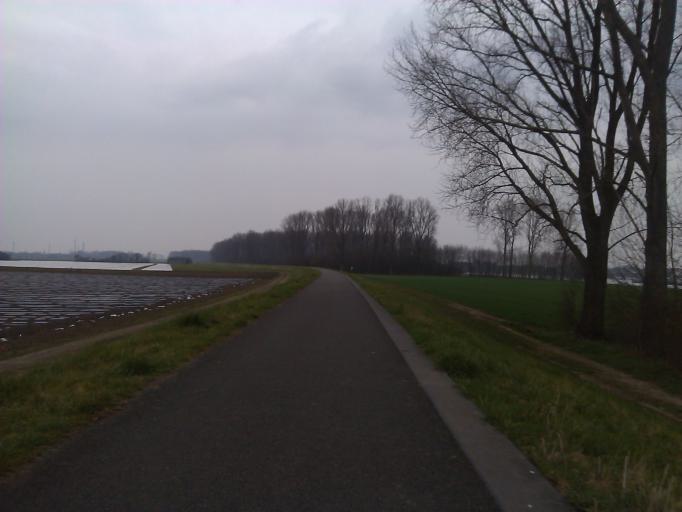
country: DE
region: North Rhine-Westphalia
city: Monheim am Rhein
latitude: 51.0530
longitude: 6.9128
